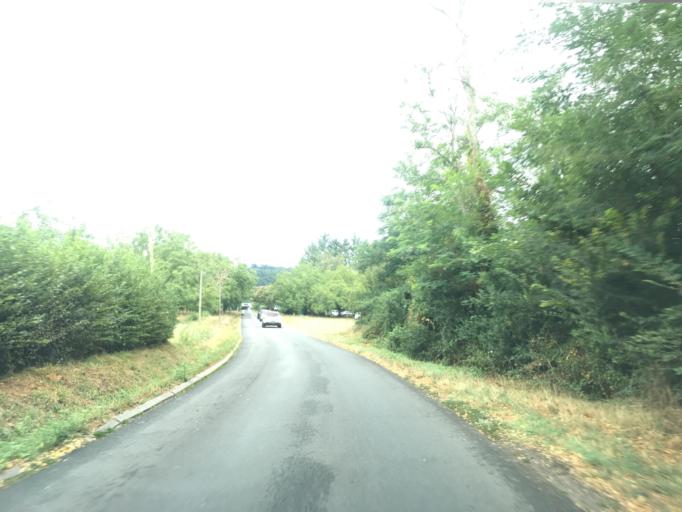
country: FR
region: Aquitaine
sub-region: Departement de la Dordogne
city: Domme
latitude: 44.8169
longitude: 1.2247
